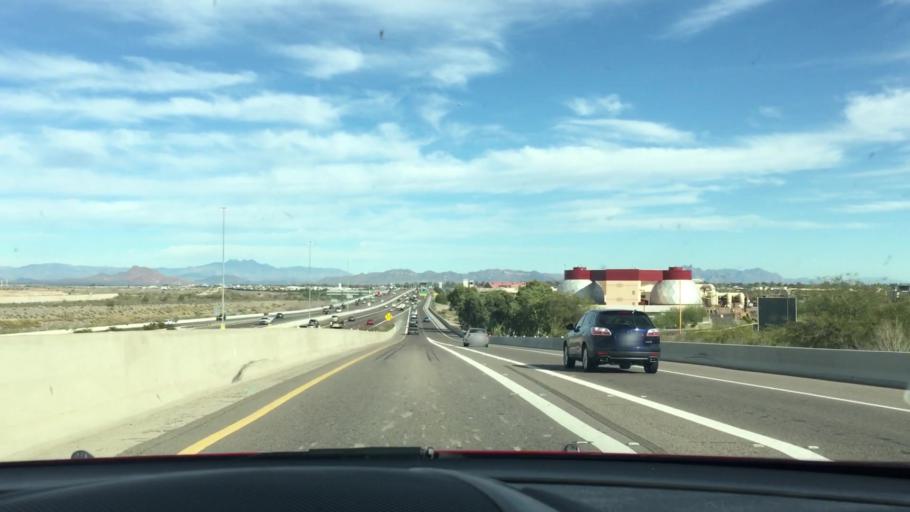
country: US
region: Arizona
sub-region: Maricopa County
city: Tempe
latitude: 33.4320
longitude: -111.8862
